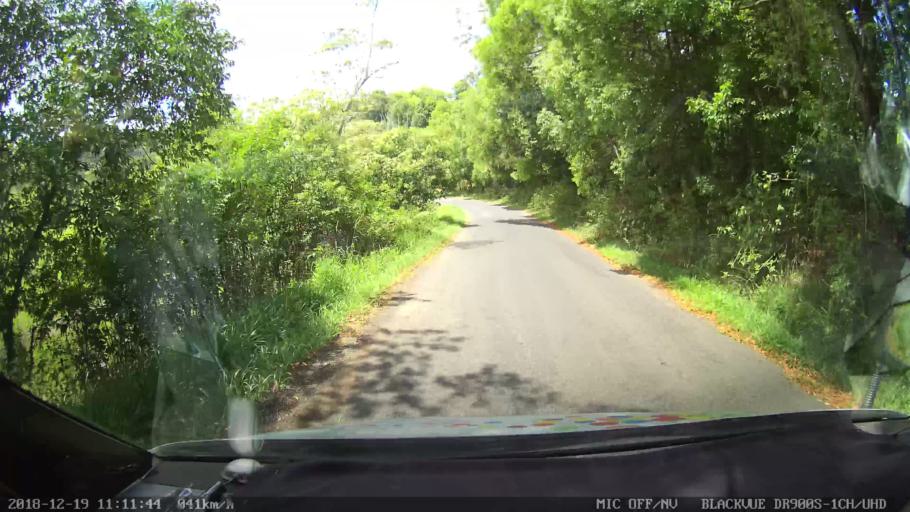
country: AU
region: New South Wales
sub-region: Lismore Municipality
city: Nimbin
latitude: -28.6450
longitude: 153.2588
